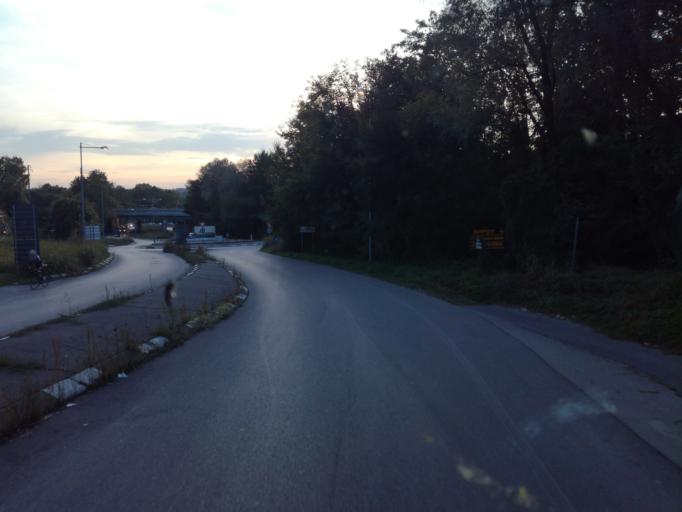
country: IT
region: Lombardy
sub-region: Provincia di Lecco
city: Nibionno
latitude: 45.7496
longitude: 9.2659
